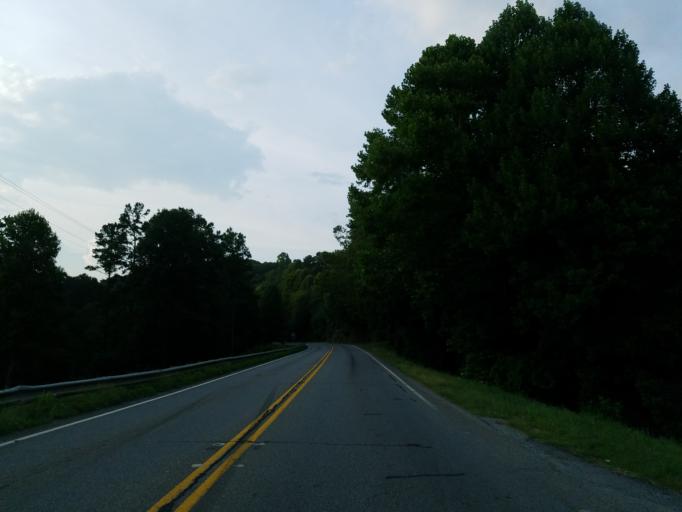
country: US
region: Georgia
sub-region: Gilmer County
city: Ellijay
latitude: 34.6815
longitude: -84.4575
